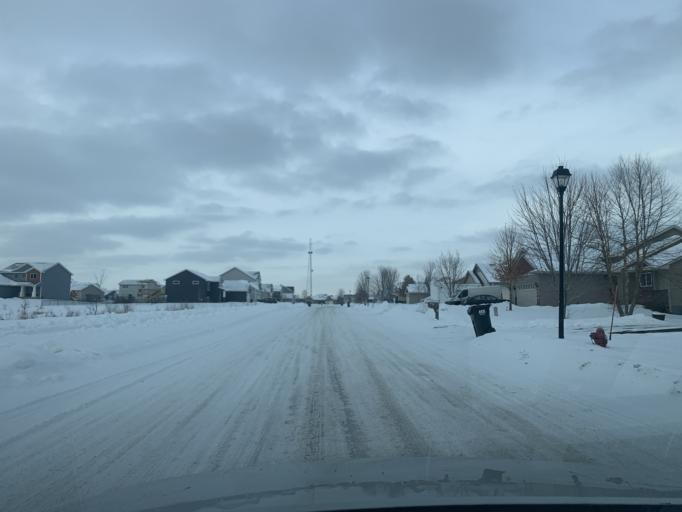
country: US
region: Minnesota
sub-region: Anoka County
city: Ramsey
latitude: 45.2440
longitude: -93.4097
